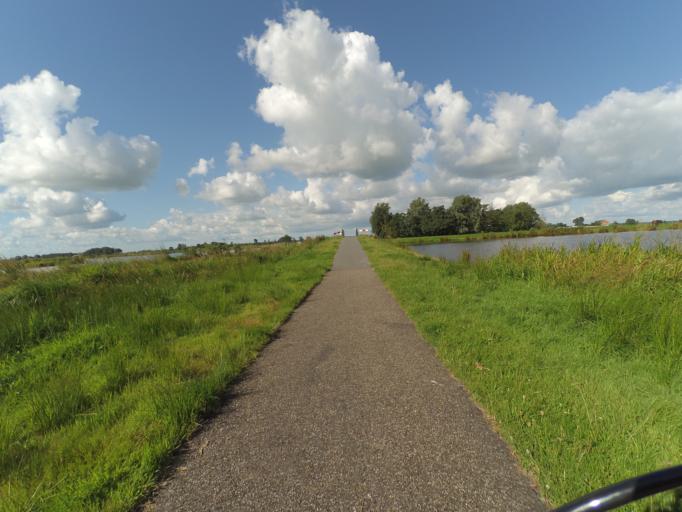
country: NL
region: Friesland
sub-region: Gemeente Dantumadiel
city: Feanwalden
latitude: 53.2517
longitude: 5.9771
